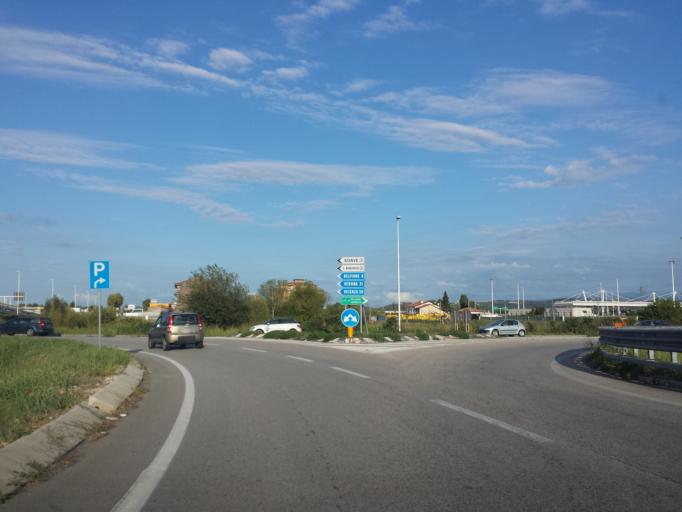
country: IT
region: Veneto
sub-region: Provincia di Verona
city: Soave
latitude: 45.4048
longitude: 11.2551
